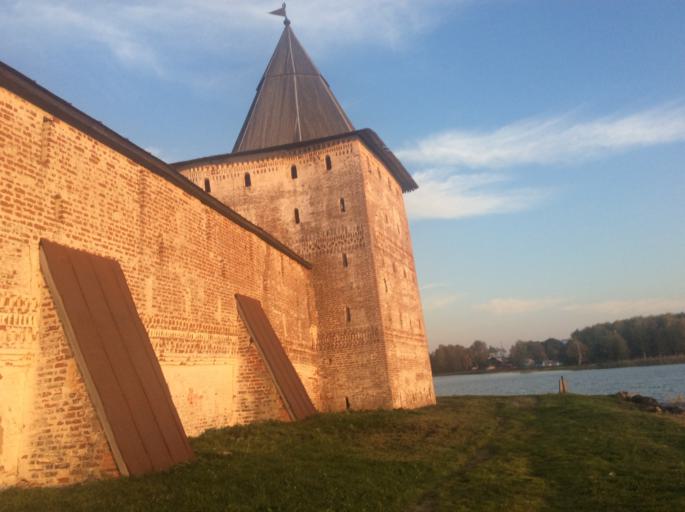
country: RU
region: Vologda
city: Kirillov
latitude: 59.8563
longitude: 38.3665
